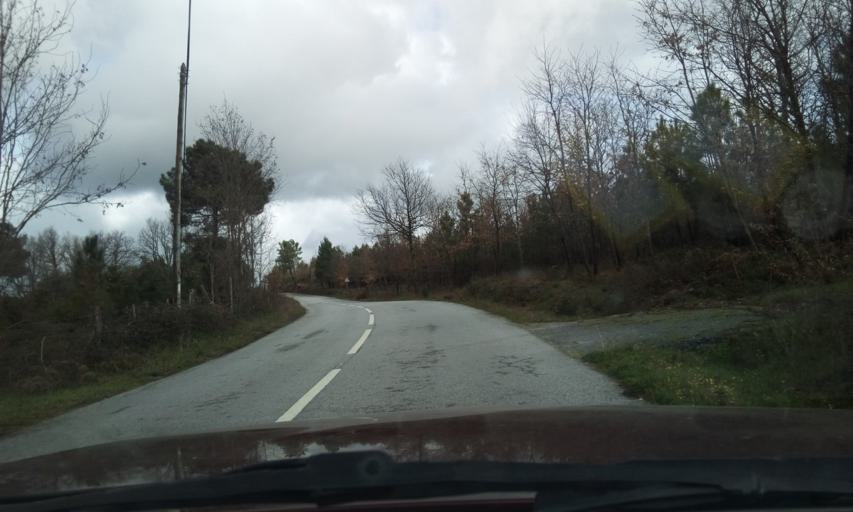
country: PT
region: Guarda
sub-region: Fornos de Algodres
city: Fornos de Algodres
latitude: 40.6366
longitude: -7.5479
